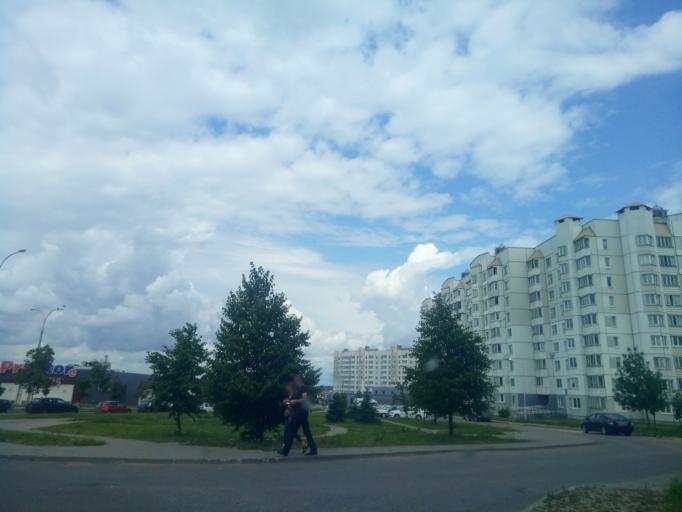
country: BY
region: Minsk
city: Zhdanovichy
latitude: 53.9101
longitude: 27.4187
